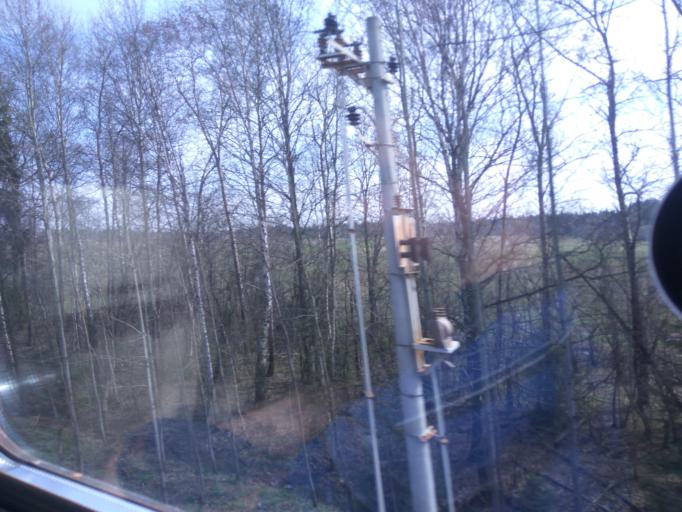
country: RU
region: Moskovskaya
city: Lugovaya
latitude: 56.0391
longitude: 37.4900
